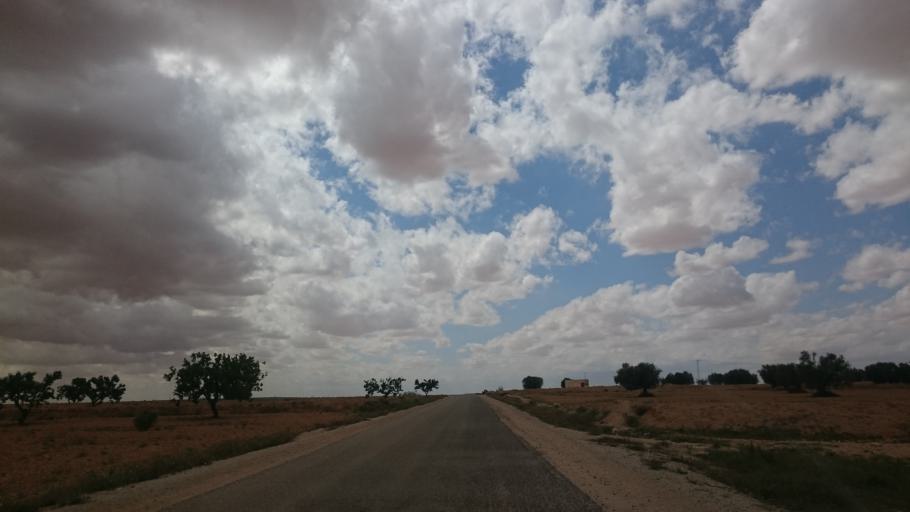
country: TN
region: Safaqis
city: Bi'r `Ali Bin Khalifah
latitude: 34.7804
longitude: 10.3817
